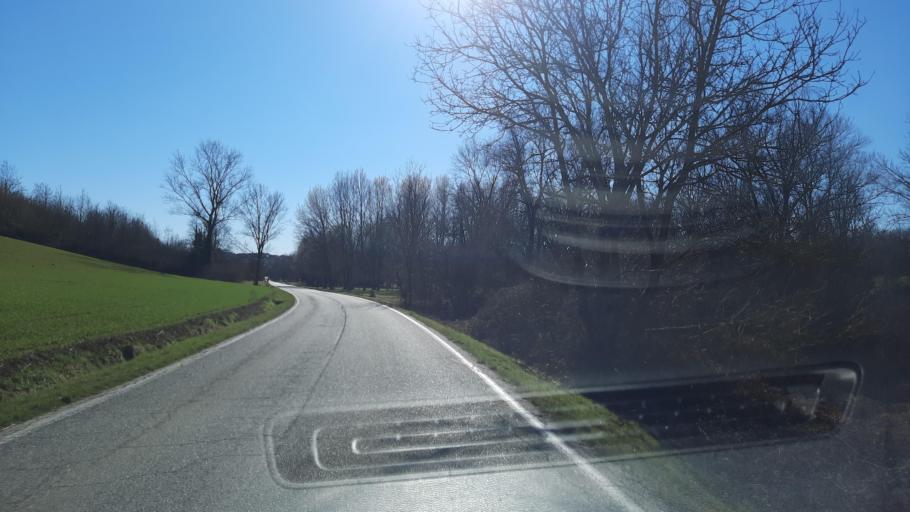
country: IT
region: Piedmont
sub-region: Provincia di Alessandria
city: Cella Monte
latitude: 45.0625
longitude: 8.4005
